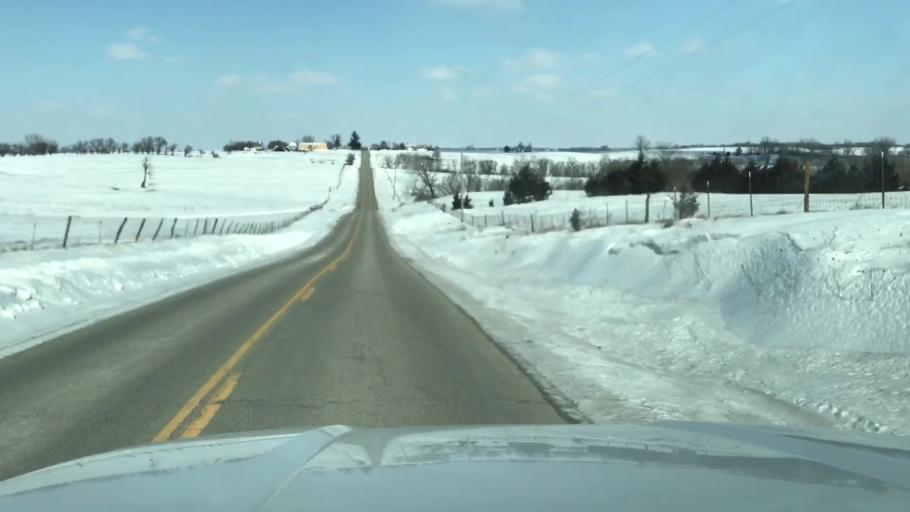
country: US
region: Missouri
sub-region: Nodaway County
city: Maryville
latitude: 40.3743
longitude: -94.7215
